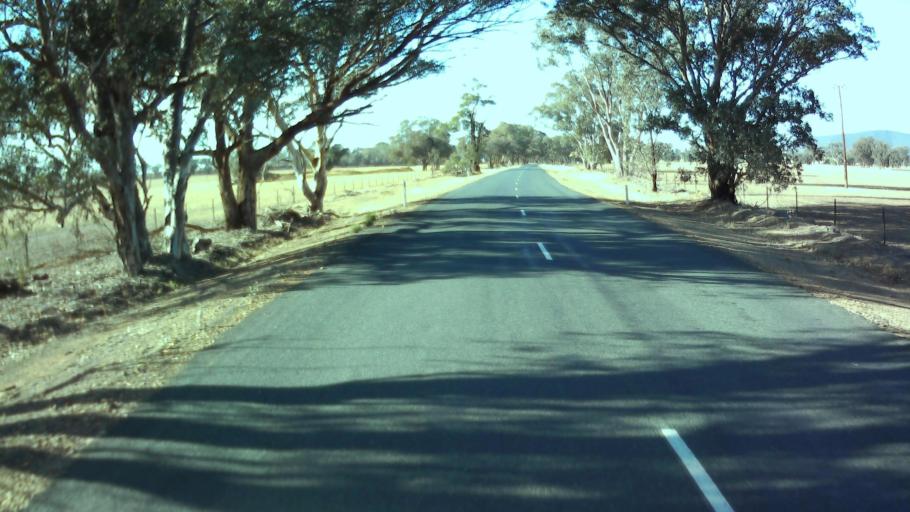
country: AU
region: New South Wales
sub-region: Weddin
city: Grenfell
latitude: -33.9351
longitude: 148.1378
